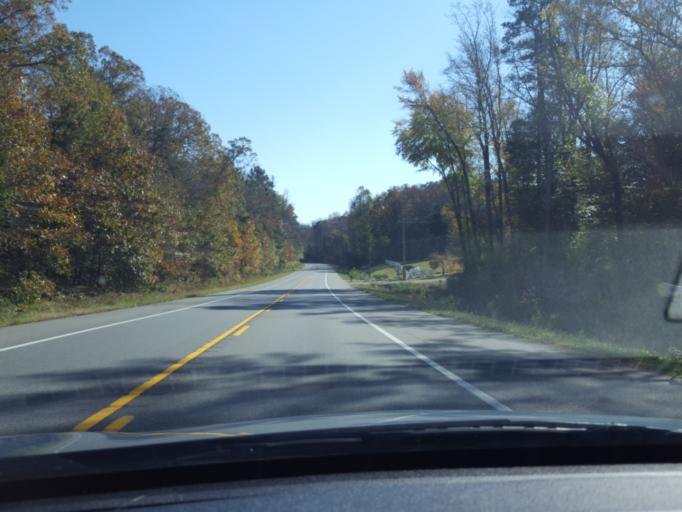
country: US
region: Maryland
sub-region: Saint Mary's County
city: Leonardtown
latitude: 38.2674
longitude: -76.6069
